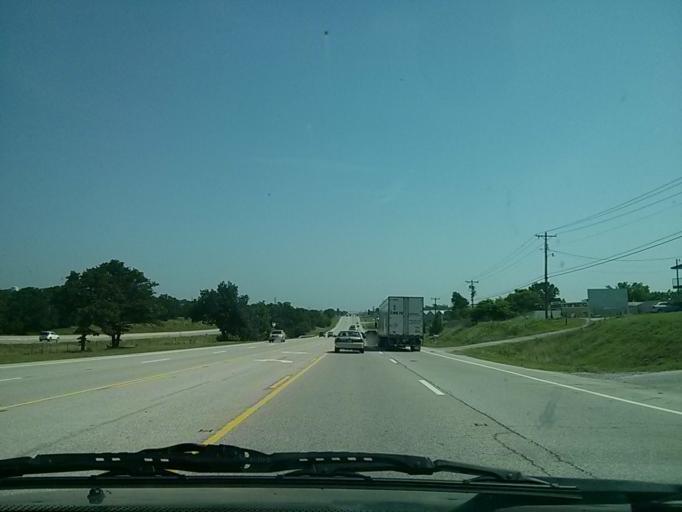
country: US
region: Oklahoma
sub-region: Tulsa County
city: Oakhurst
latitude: 36.0395
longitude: -96.0824
